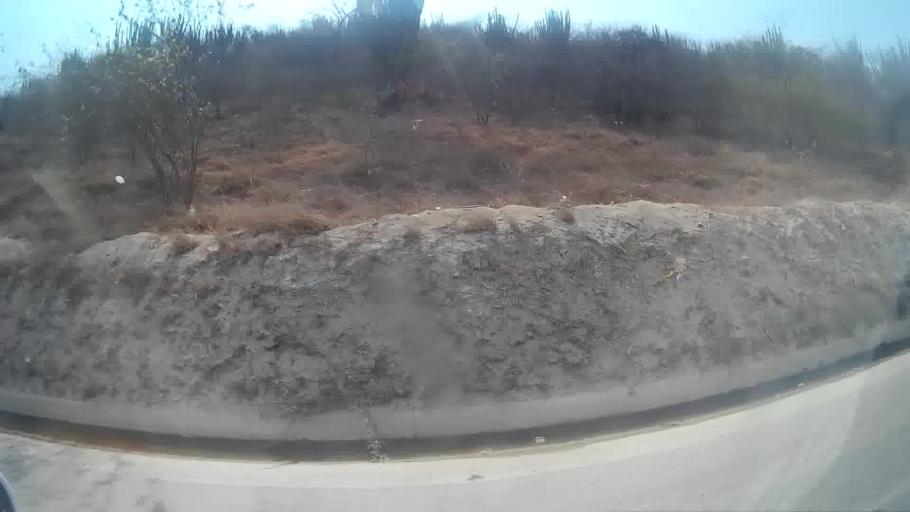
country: CO
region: Magdalena
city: Santa Marta
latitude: 11.1950
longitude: -74.2046
